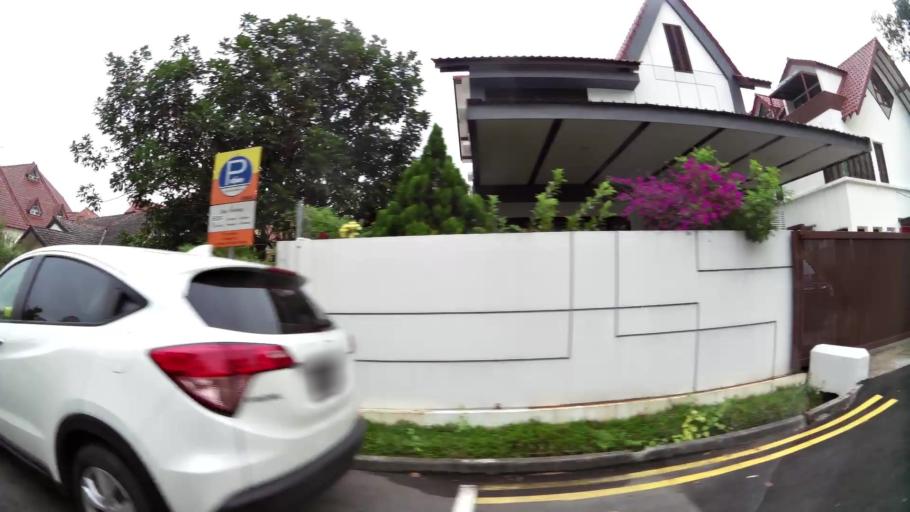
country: SG
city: Singapore
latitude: 1.3309
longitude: 103.8705
